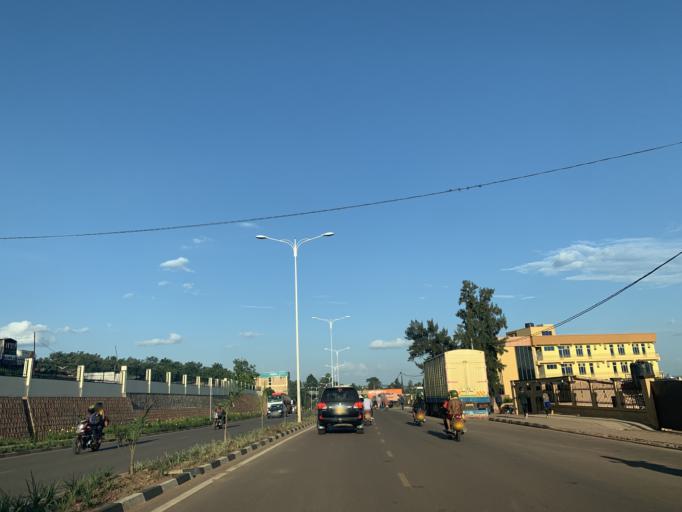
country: RW
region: Kigali
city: Kigali
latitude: -1.9605
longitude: 30.1145
